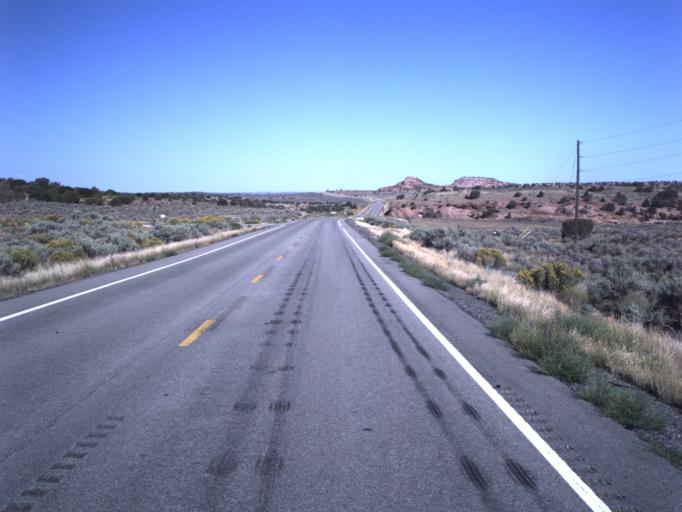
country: US
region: Utah
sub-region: Grand County
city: Moab
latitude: 38.3011
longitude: -109.3939
